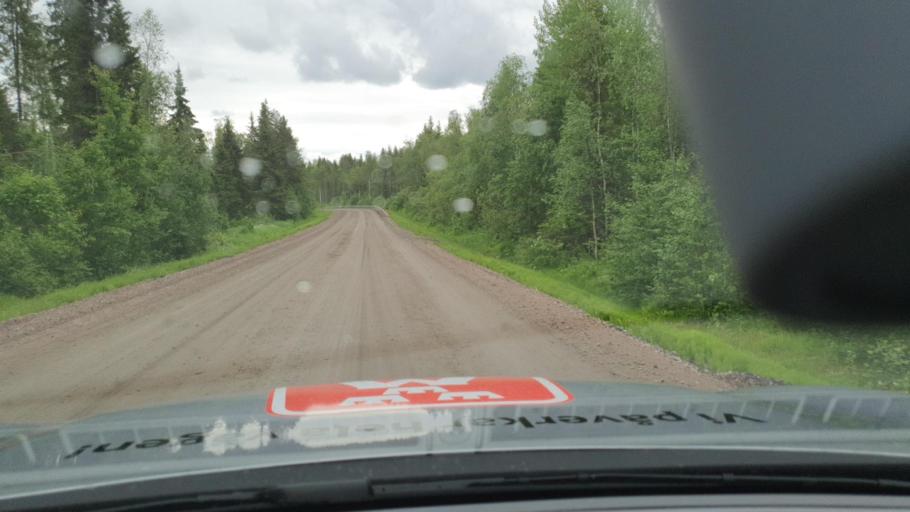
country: SE
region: Norrbotten
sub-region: Overtornea Kommun
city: OEvertornea
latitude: 66.4187
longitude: 23.5763
